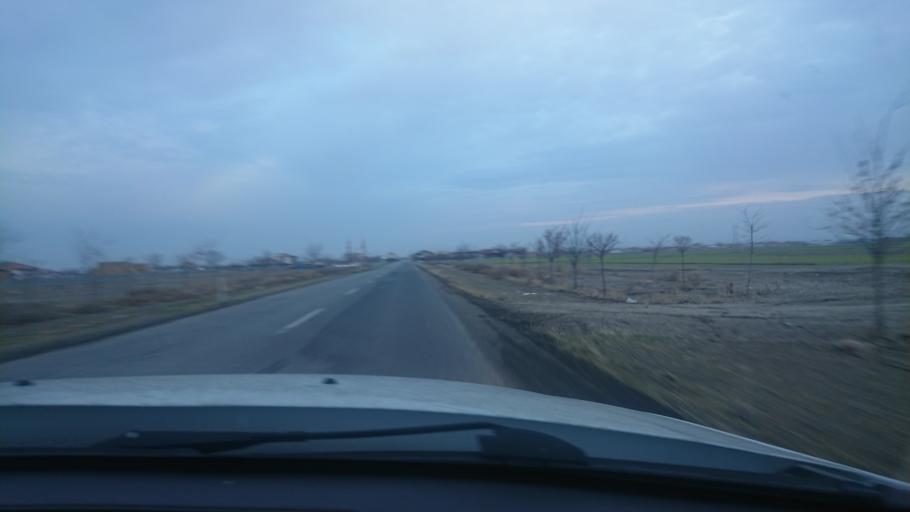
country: TR
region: Aksaray
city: Yesilova
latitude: 38.3281
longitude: 33.7528
